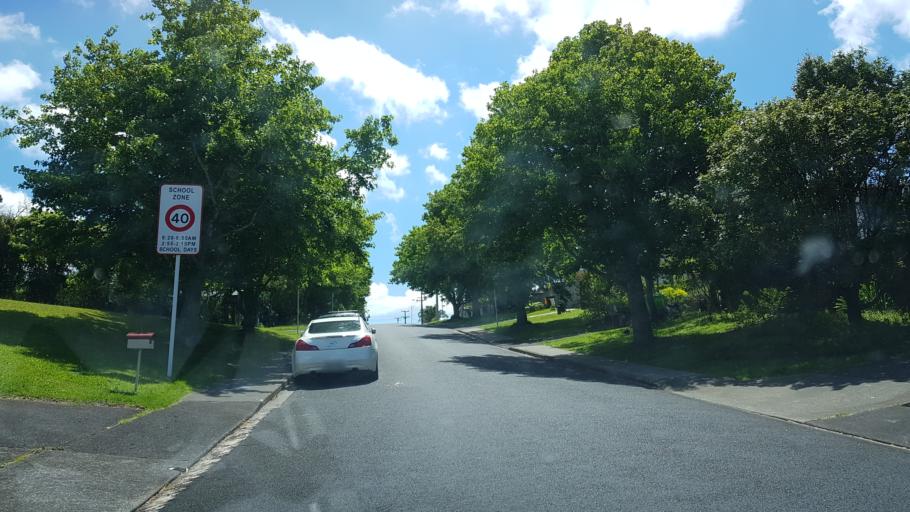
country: NZ
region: Auckland
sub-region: Auckland
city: North Shore
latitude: -36.7910
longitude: 174.7115
